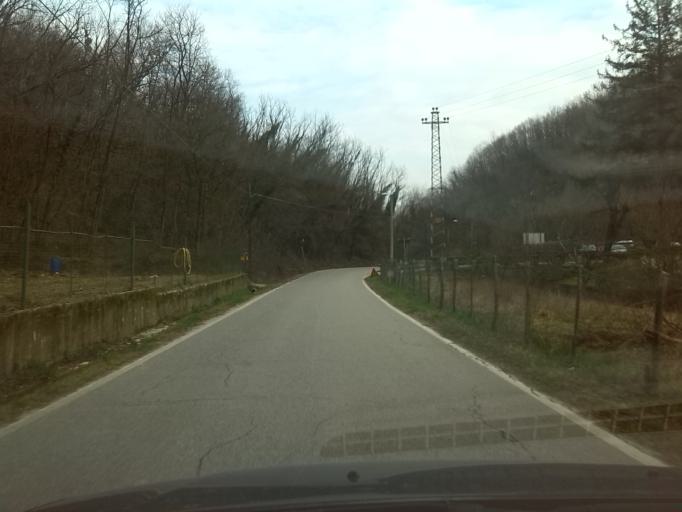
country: IT
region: Friuli Venezia Giulia
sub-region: Provincia di Gorizia
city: Gorizia
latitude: 45.9572
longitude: 13.6013
